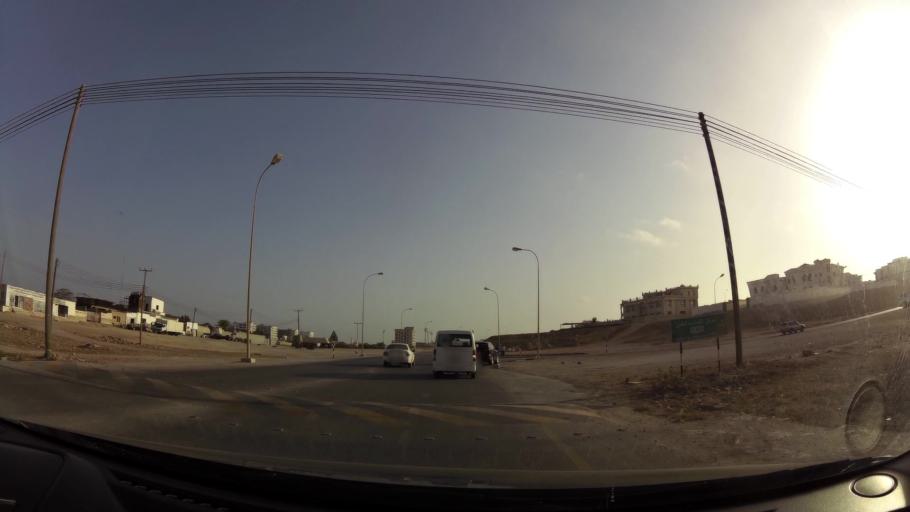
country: OM
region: Zufar
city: Salalah
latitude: 17.0010
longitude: 54.0314
